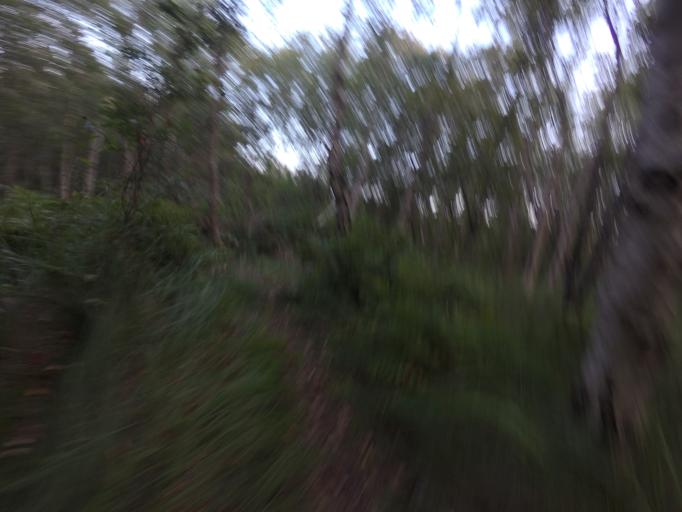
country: NL
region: Friesland
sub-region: Gemeente Schiermonnikoog
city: Schiermonnikoog
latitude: 53.4905
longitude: 6.1710
